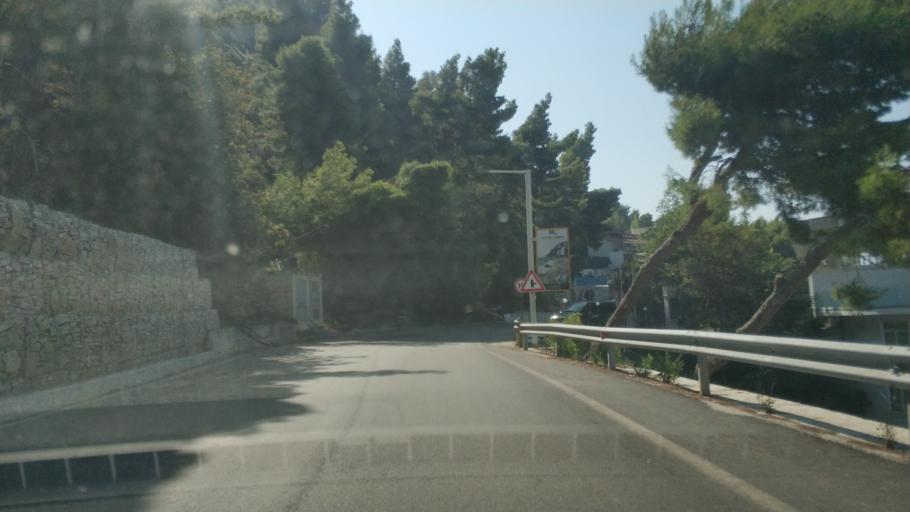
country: AL
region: Vlore
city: Vlore
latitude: 40.4071
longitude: 19.4808
